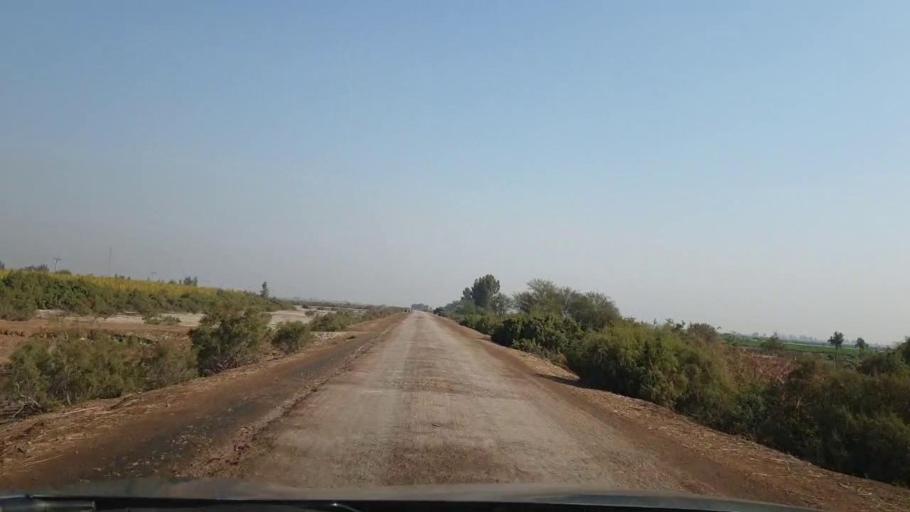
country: PK
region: Sindh
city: Berani
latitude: 25.6363
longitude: 68.8670
